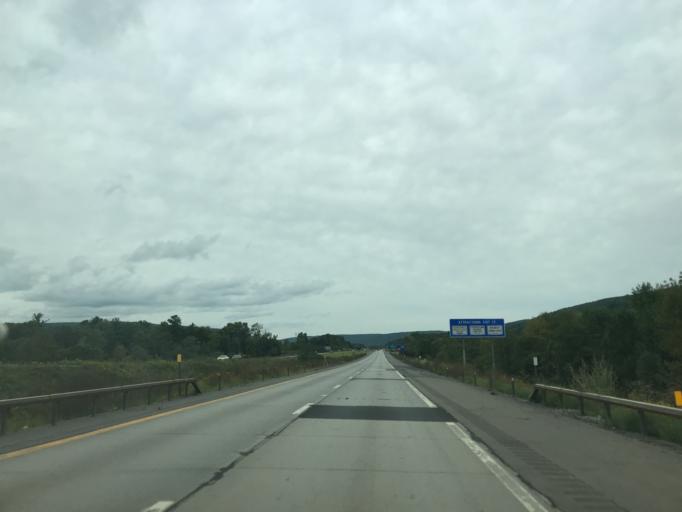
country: US
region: New York
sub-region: Otsego County
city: Oneonta
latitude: 42.4767
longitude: -74.9886
